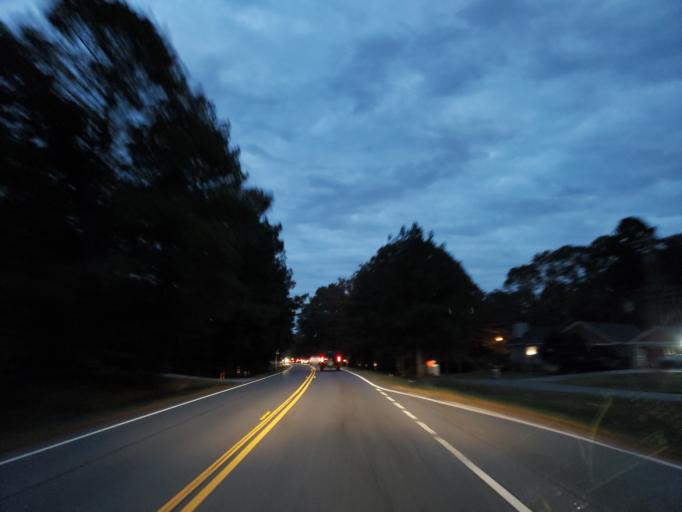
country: US
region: Georgia
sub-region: Cobb County
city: Powder Springs
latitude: 33.9110
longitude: -84.6850
